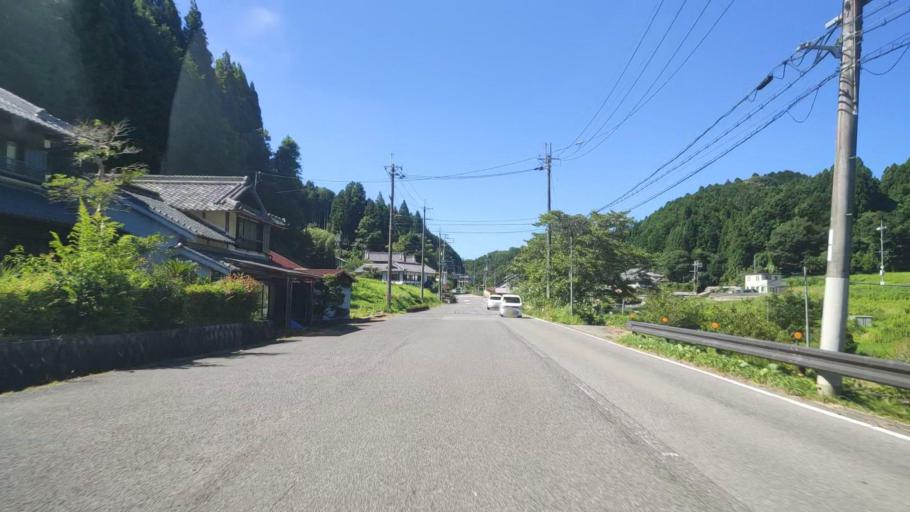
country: JP
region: Nara
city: Haibara-akanedai
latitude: 34.4452
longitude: 135.9379
